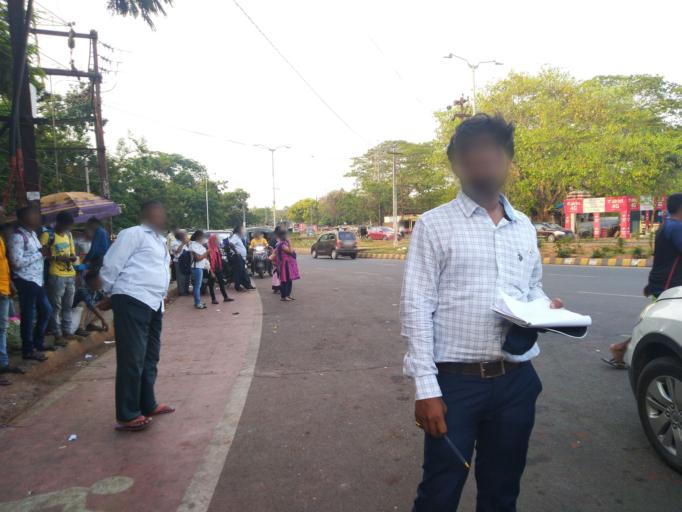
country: IN
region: Odisha
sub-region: Khordha
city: Bhubaneshwar
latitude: 20.2973
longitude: 85.8330
